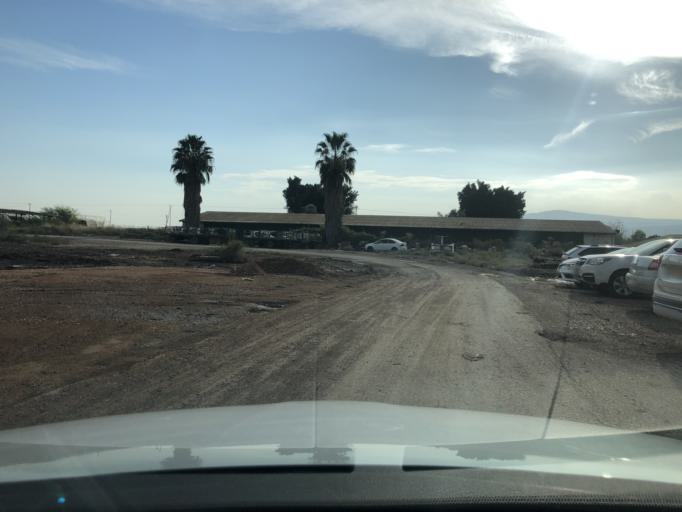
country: IL
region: Northern District
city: Yavne'el
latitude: 32.6567
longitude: 35.5815
